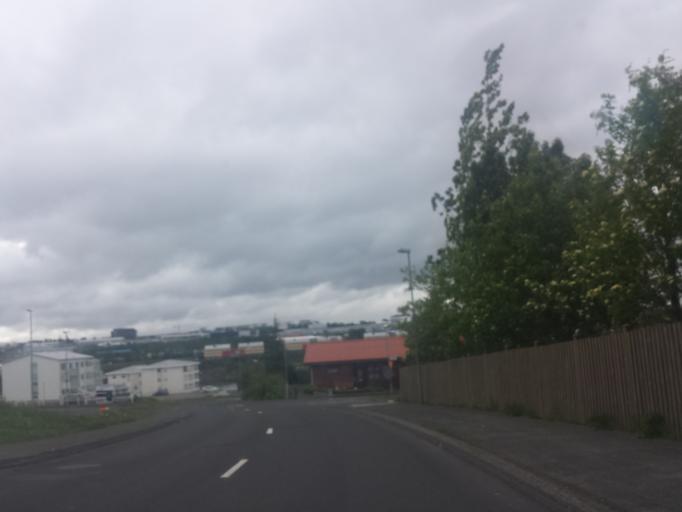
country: IS
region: Capital Region
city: Reykjavik
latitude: 64.1350
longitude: -21.7997
